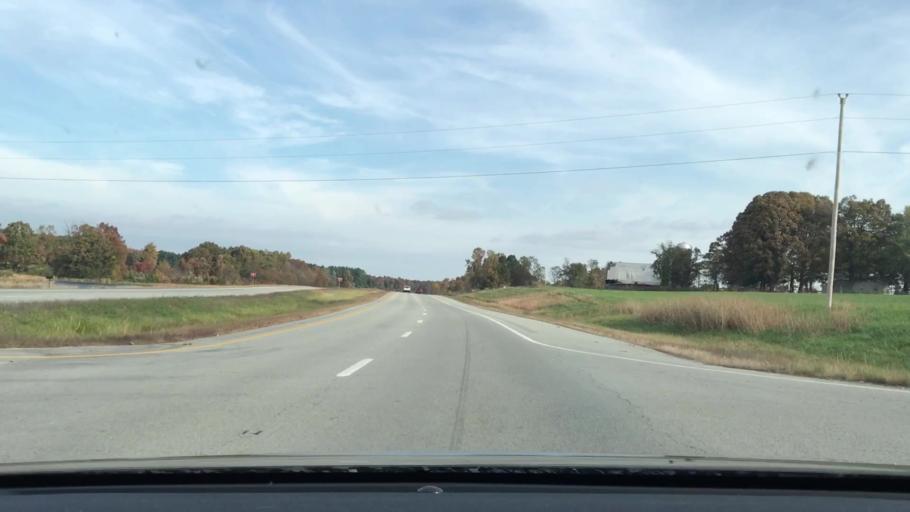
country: US
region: Tennessee
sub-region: Fentress County
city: Grimsley
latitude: 36.3203
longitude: -84.9643
